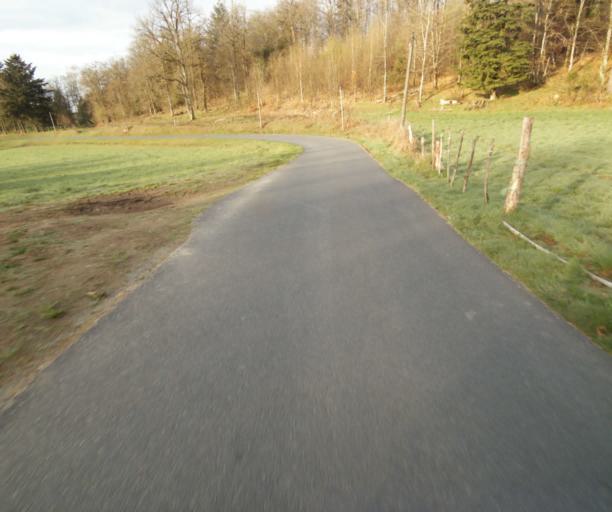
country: FR
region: Limousin
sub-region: Departement de la Correze
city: Correze
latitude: 45.4065
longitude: 1.8731
